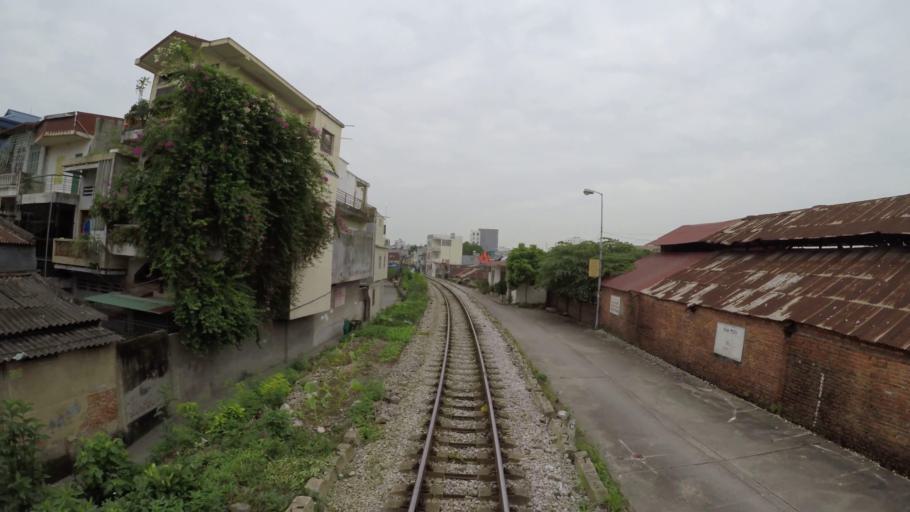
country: VN
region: Hai Phong
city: Haiphong
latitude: 20.8702
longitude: 106.6530
